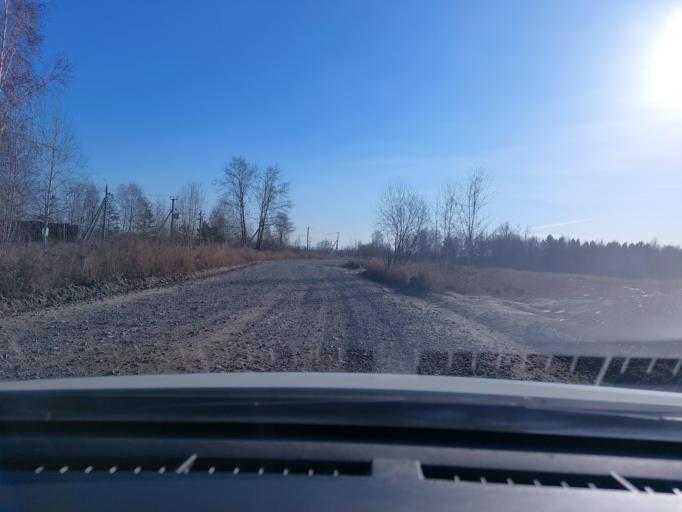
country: RU
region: Irkutsk
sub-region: Irkutskiy Rayon
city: Irkutsk
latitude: 52.3069
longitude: 104.2732
